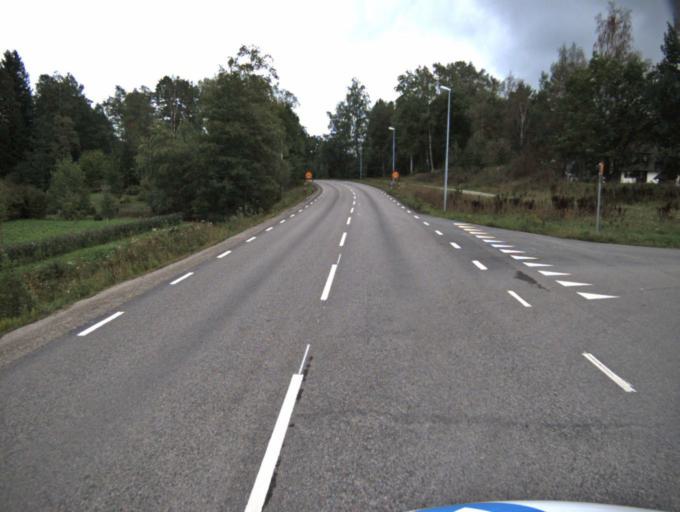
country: SE
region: Vaestra Goetaland
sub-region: Ulricehamns Kommun
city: Ulricehamn
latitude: 57.7783
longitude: 13.4249
